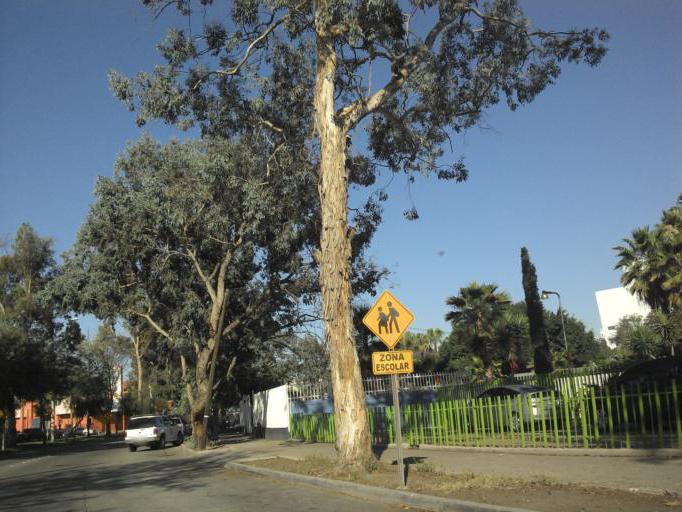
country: MX
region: Baja California
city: Tijuana
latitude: 32.5169
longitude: -117.0059
